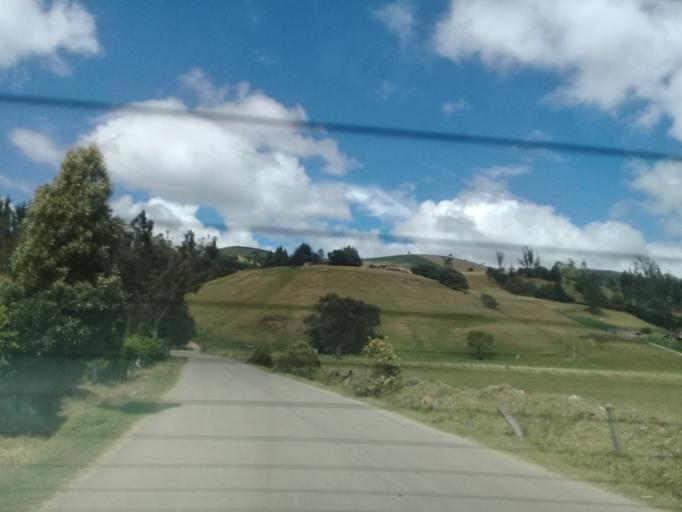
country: CO
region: Cundinamarca
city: Choconta
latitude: 5.1493
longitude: -73.6926
